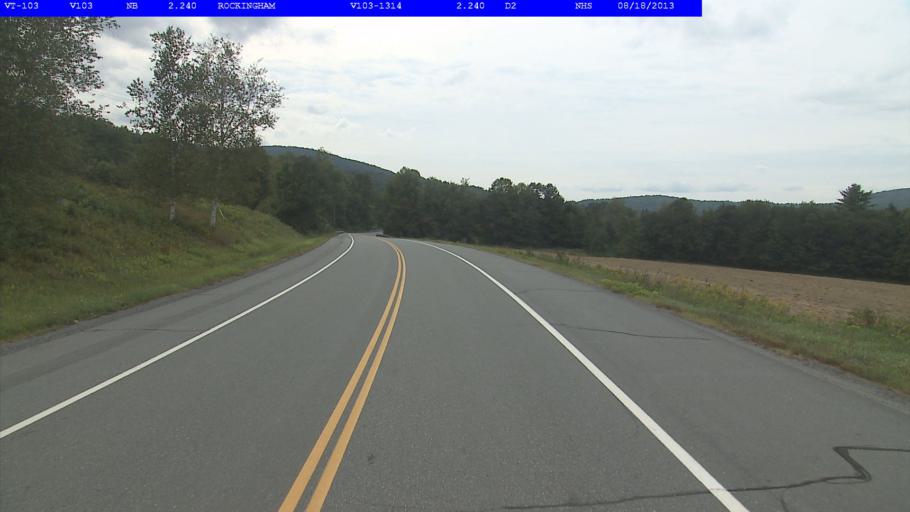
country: US
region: Vermont
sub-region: Windham County
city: Rockingham
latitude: 43.1945
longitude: -72.4966
